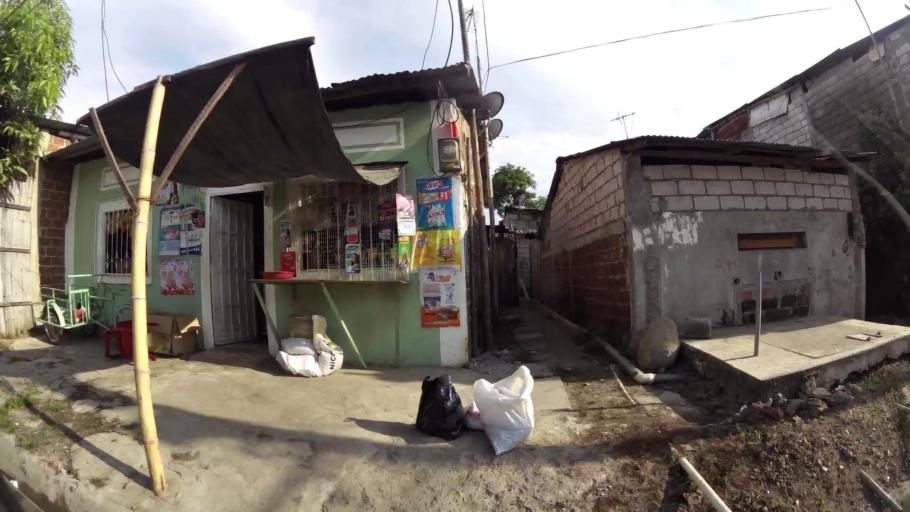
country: EC
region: Guayas
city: Eloy Alfaro
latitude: -2.0776
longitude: -79.9257
